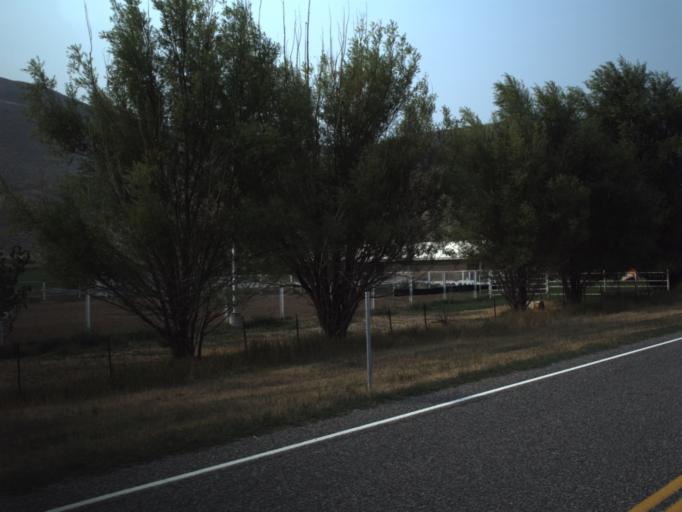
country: US
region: Utah
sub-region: Summit County
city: Coalville
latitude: 41.0174
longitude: -111.5085
